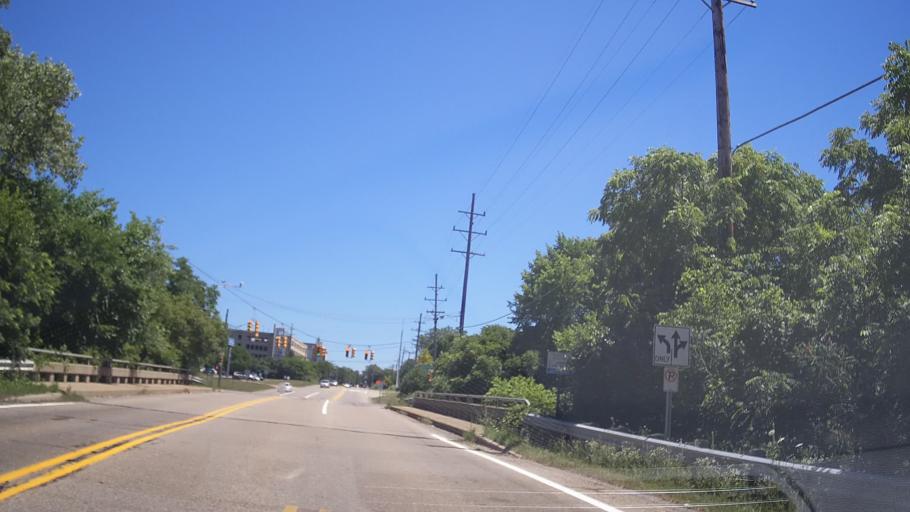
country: US
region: Michigan
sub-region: Macomb County
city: Clinton
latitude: 42.5879
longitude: -82.9043
